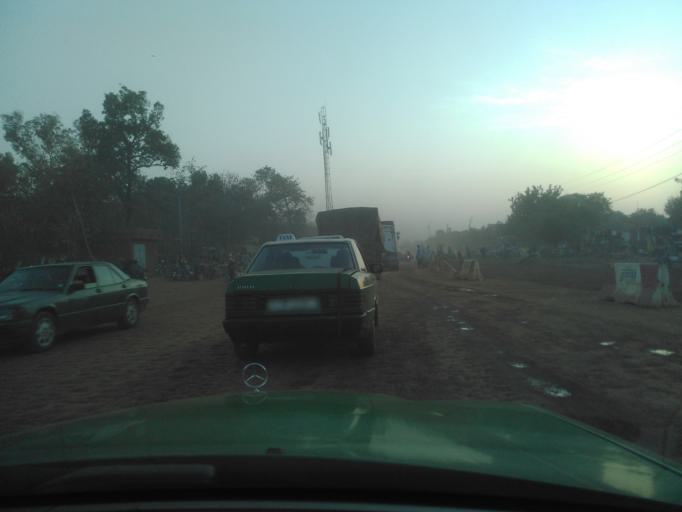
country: BF
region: Centre
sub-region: Kadiogo Province
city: Ouagadougou
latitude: 12.3829
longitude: -1.5052
